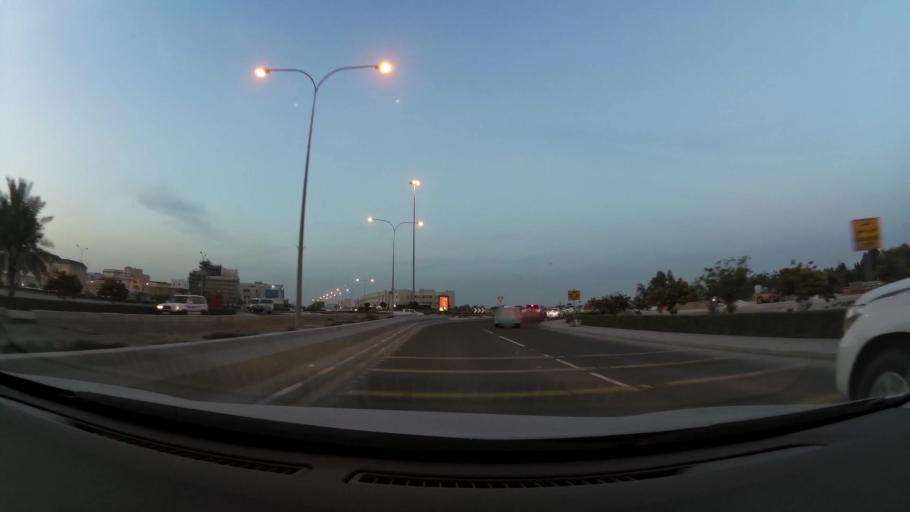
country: QA
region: Al Wakrah
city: Al Wakrah
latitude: 25.1610
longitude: 51.6075
